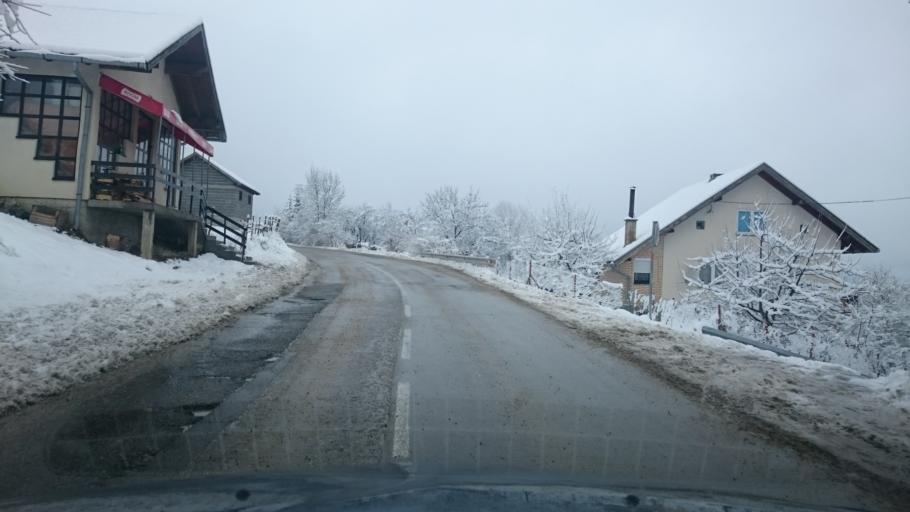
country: BA
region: Republika Srpska
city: Zivinice
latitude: 44.5210
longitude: 17.3029
